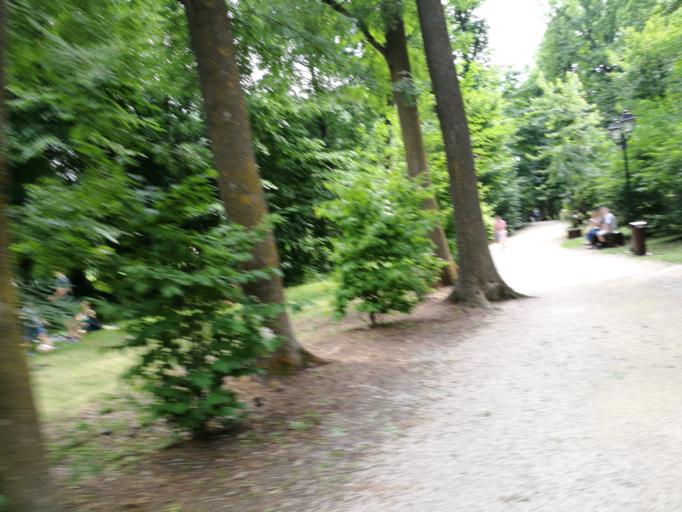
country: RO
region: Ilfov
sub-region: Comuna Mogosoaia
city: Mogosoaia
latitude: 44.5266
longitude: 25.9962
